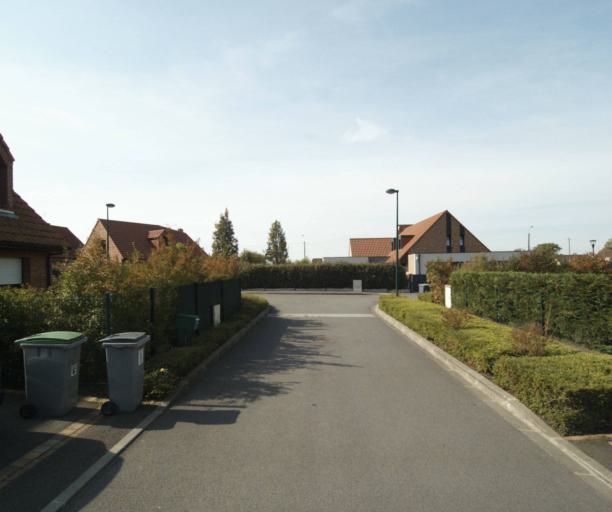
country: FR
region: Nord-Pas-de-Calais
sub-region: Departement du Nord
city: Capinghem
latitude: 50.6449
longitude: 2.9556
